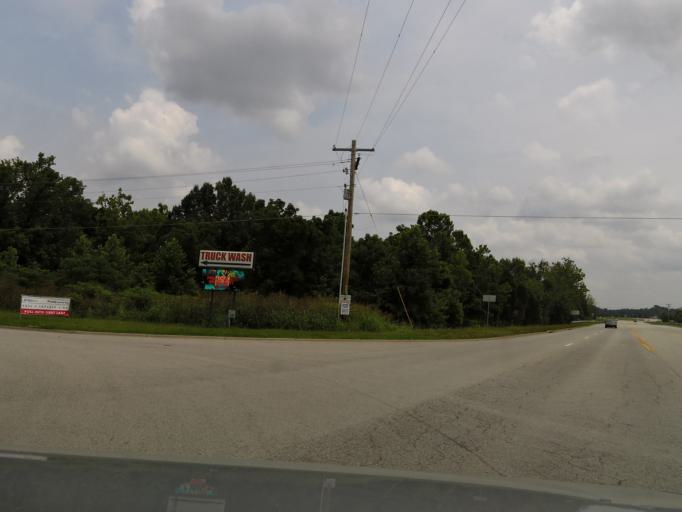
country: US
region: Kentucky
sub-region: Bullitt County
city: Shepherdsville
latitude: 37.9786
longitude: -85.6933
